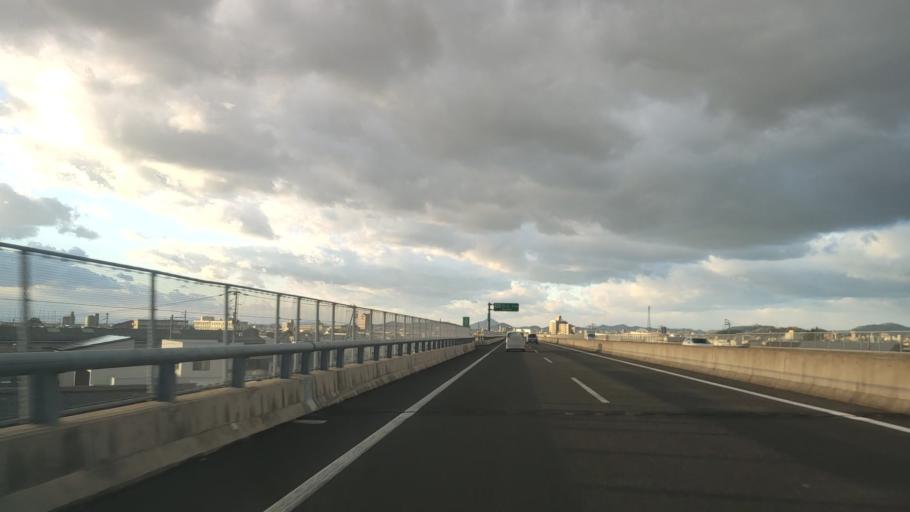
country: JP
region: Ehime
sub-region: Shikoku-chuo Shi
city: Matsuyama
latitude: 33.7912
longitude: 132.8035
